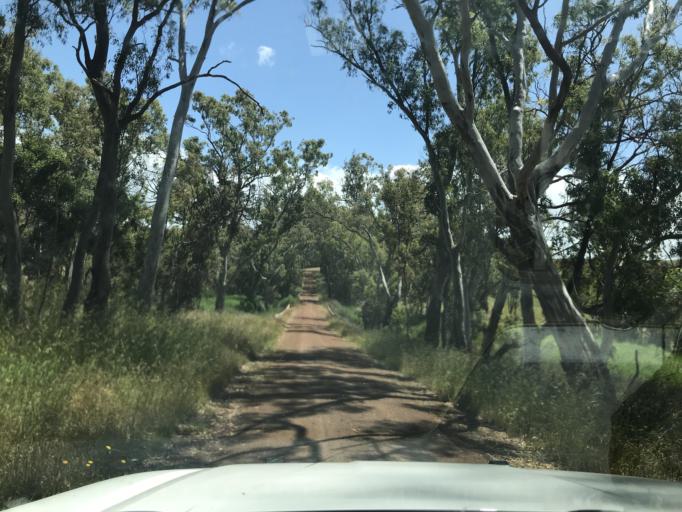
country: AU
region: South Australia
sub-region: Wattle Range
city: Penola
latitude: -37.2875
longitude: 141.4849
